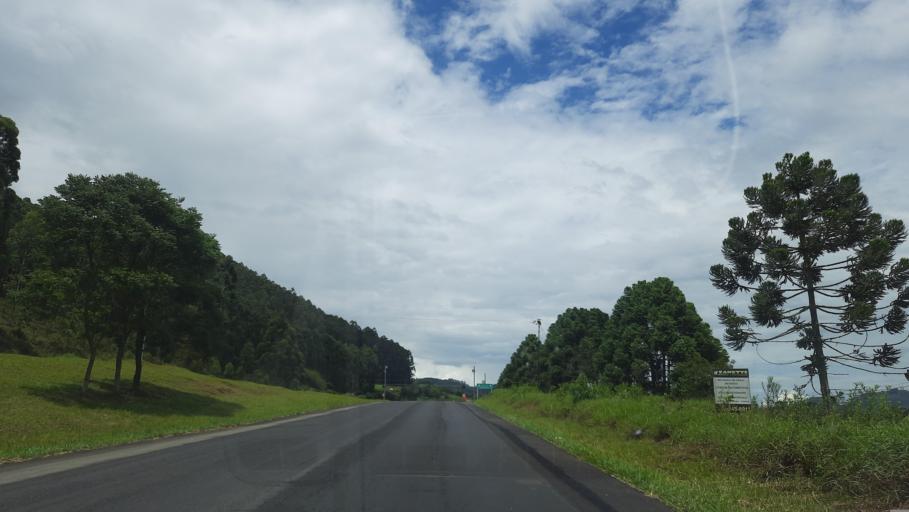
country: BR
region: Minas Gerais
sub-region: Pocos De Caldas
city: Pocos de Caldas
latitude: -21.8008
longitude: -46.6495
